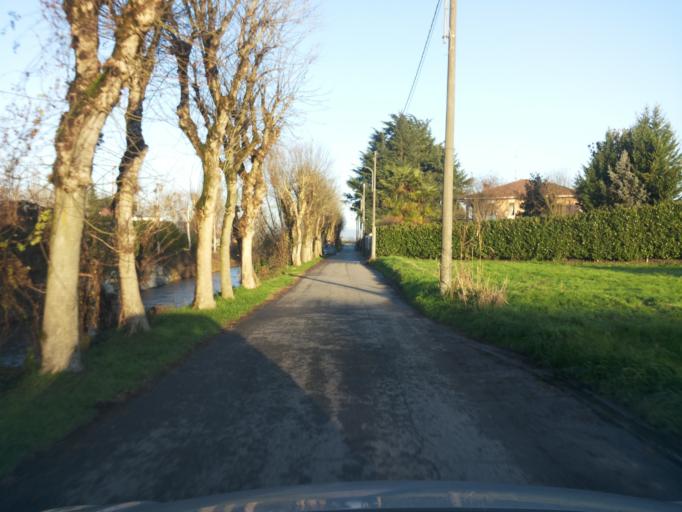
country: IT
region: Piedmont
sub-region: Provincia di Vercelli
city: Asigliano Vercellese
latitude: 45.2601
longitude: 8.4124
